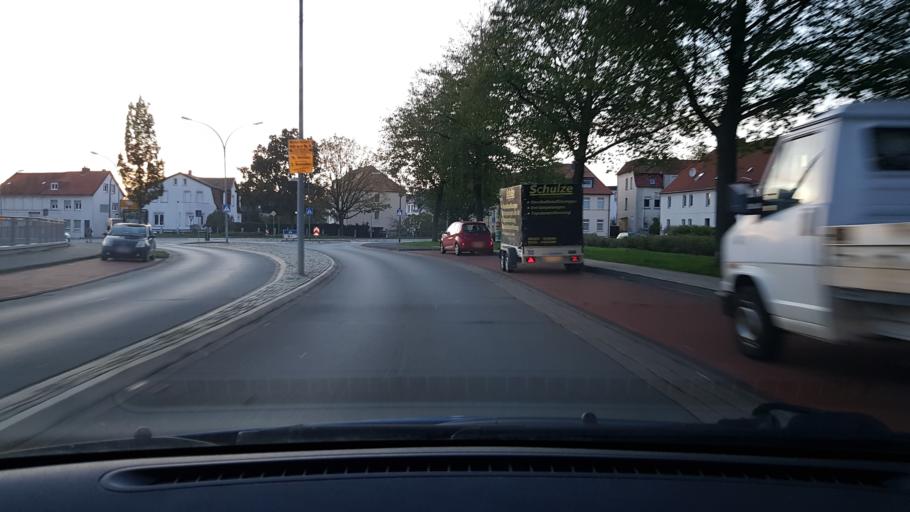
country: DE
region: Lower Saxony
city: Helmstedt
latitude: 52.2336
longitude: 11.0091
